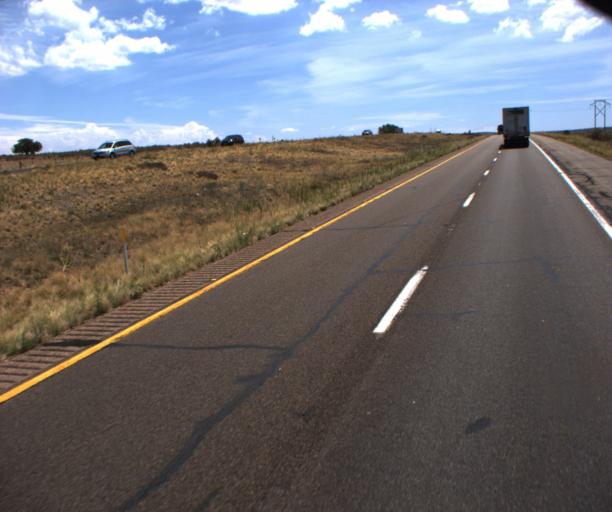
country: US
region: Arizona
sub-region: Yavapai County
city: Paulden
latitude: 35.2925
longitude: -112.8243
